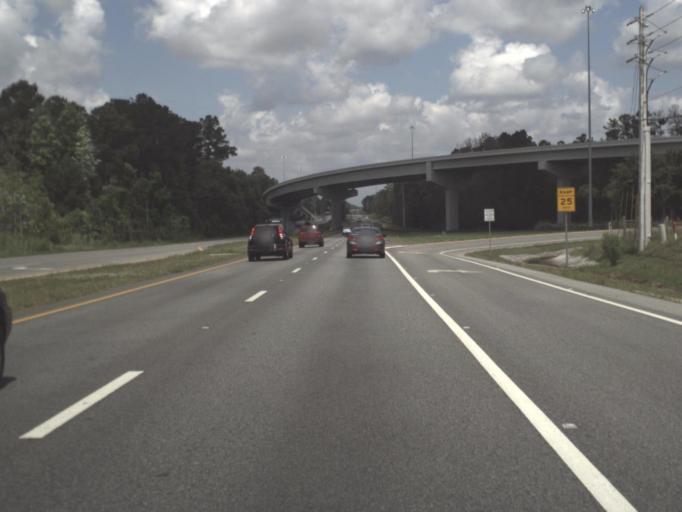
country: US
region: Florida
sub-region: Saint Johns County
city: Palm Valley
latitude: 30.0957
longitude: -81.4696
